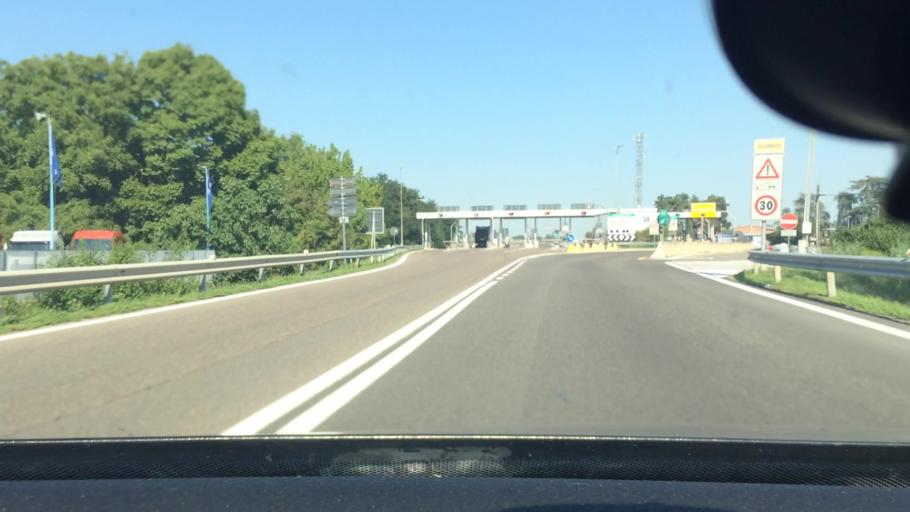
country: IT
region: Lombardy
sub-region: Provincia di Lodi
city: Guardamiglio
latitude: 45.1057
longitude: 9.6864
